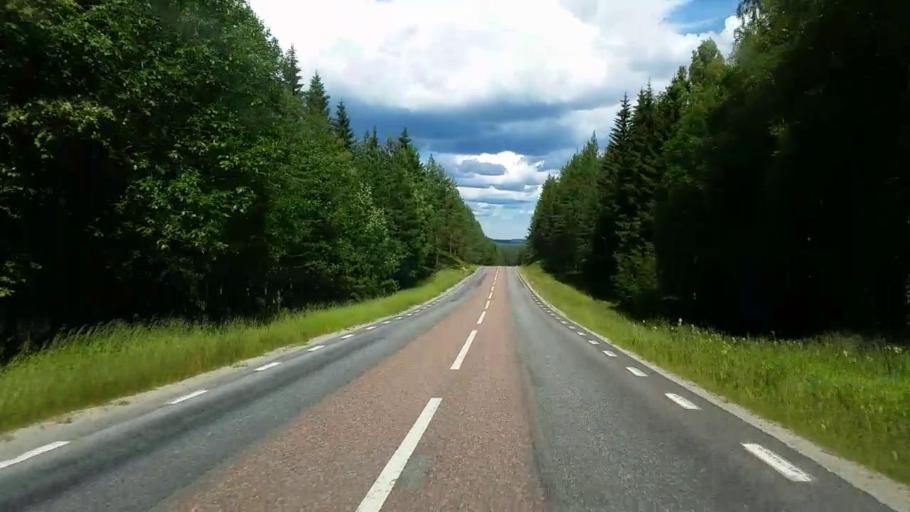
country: SE
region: Gaevleborg
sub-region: Ovanakers Kommun
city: Edsbyn
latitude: 61.3232
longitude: 15.5164
